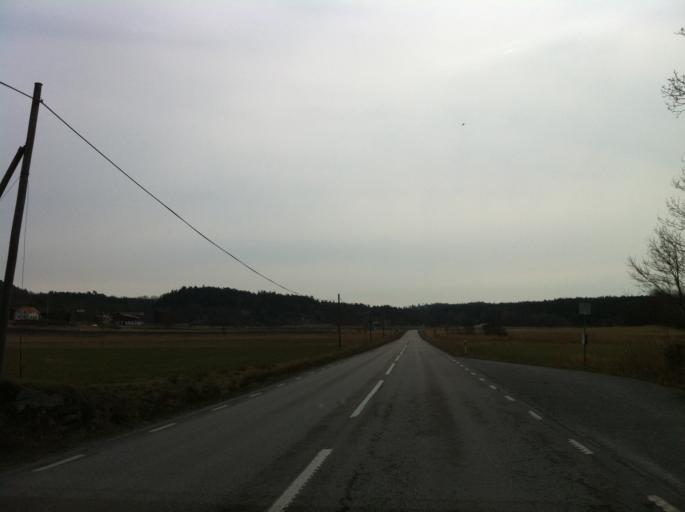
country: SE
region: Vaestra Goetaland
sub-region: Orust
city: Henan
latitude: 58.3029
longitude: 11.6997
